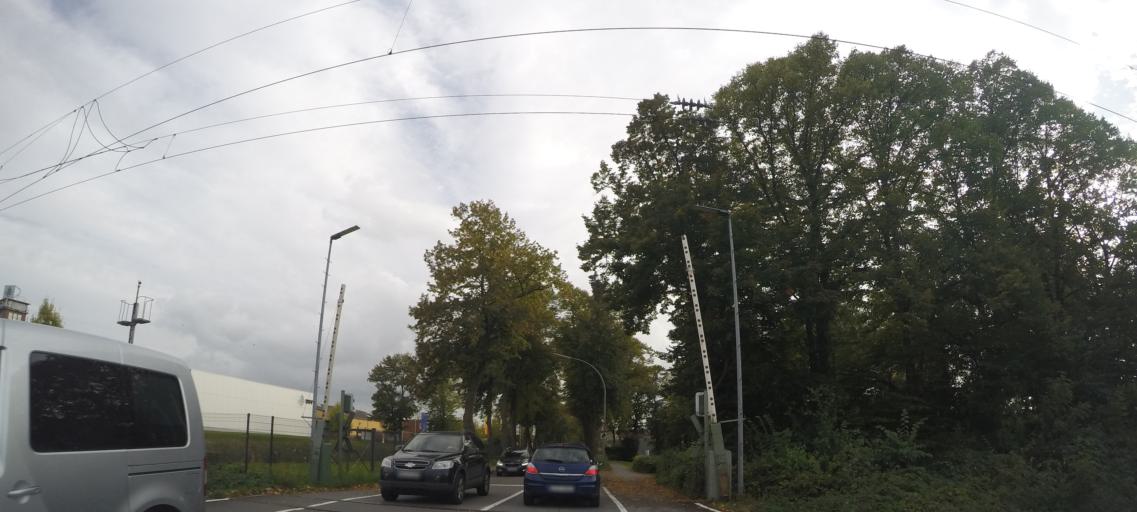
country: DE
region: North Rhine-Westphalia
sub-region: Regierungsbezirk Arnsberg
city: Lippstadt
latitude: 51.6711
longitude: 8.3569
